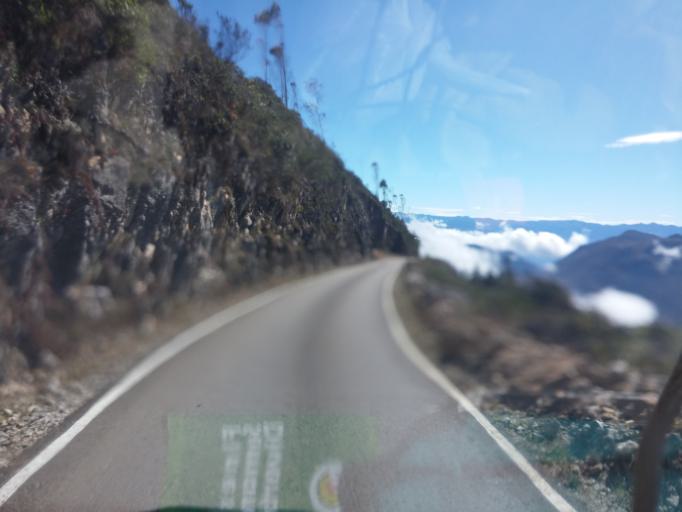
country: PE
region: Cajamarca
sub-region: Provincia de Celendin
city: Celendin
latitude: -6.8741
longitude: -78.1125
